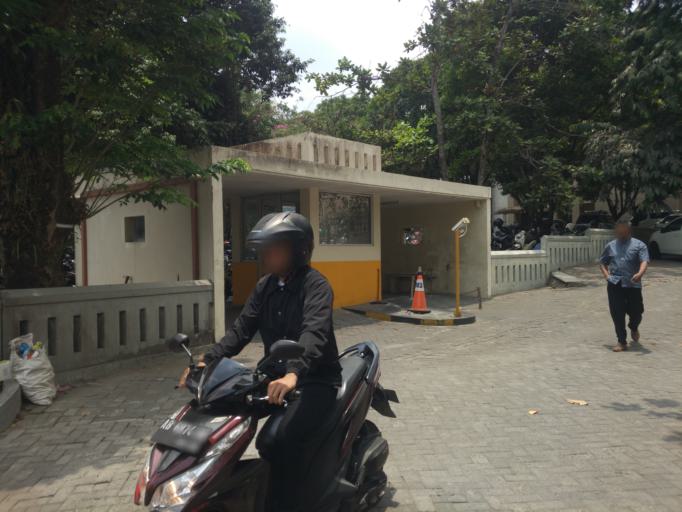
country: ID
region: Daerah Istimewa Yogyakarta
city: Sleman
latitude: -7.6877
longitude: 110.4137
